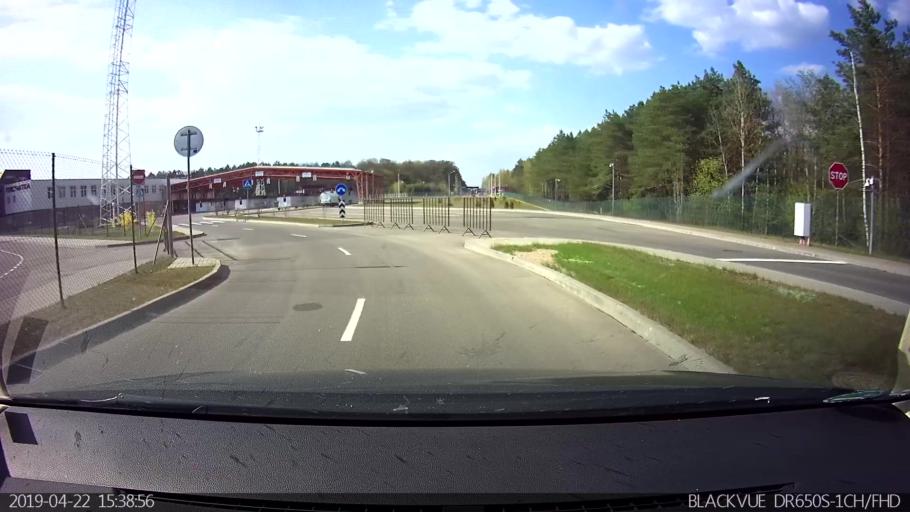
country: PL
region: Podlasie
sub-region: Powiat hajnowski
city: Czeremcha
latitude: 52.4657
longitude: 23.3608
